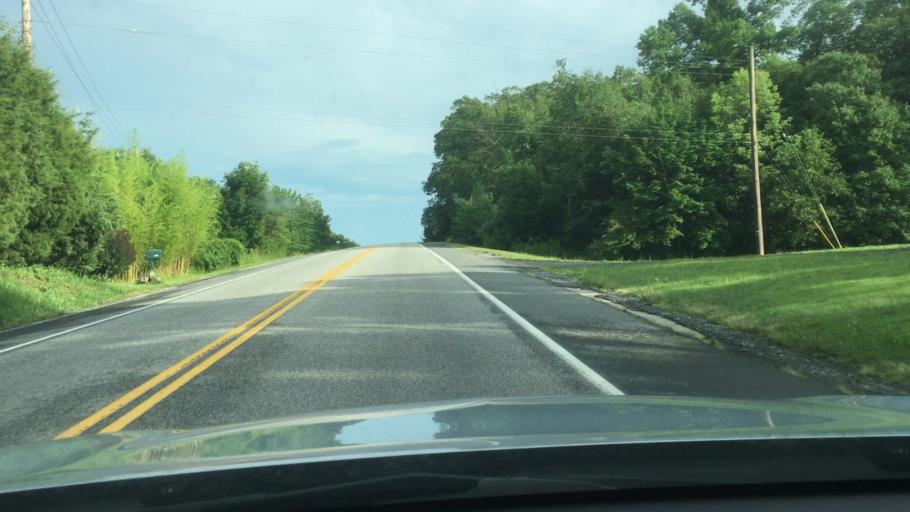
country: US
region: Pennsylvania
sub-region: York County
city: Dover
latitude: 40.0742
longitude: -76.9251
